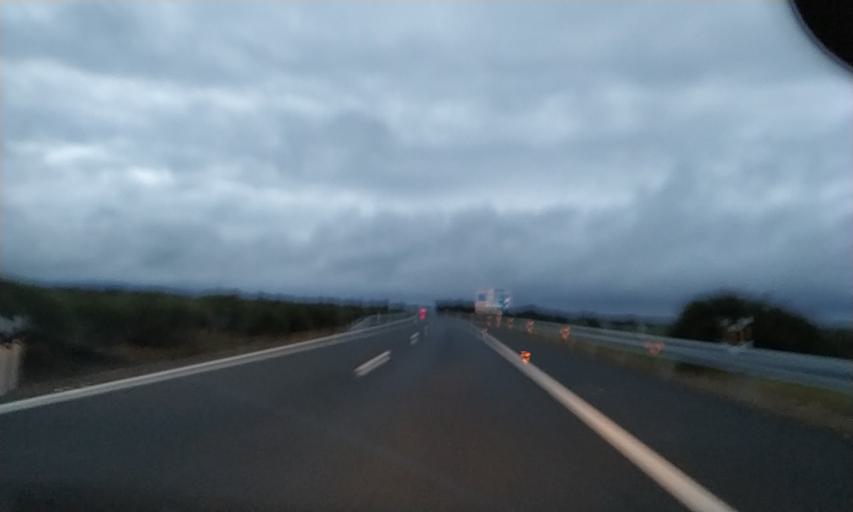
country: ES
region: Extremadura
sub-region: Provincia de Caceres
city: Casas de Don Antonio
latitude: 39.2181
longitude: -6.2916
